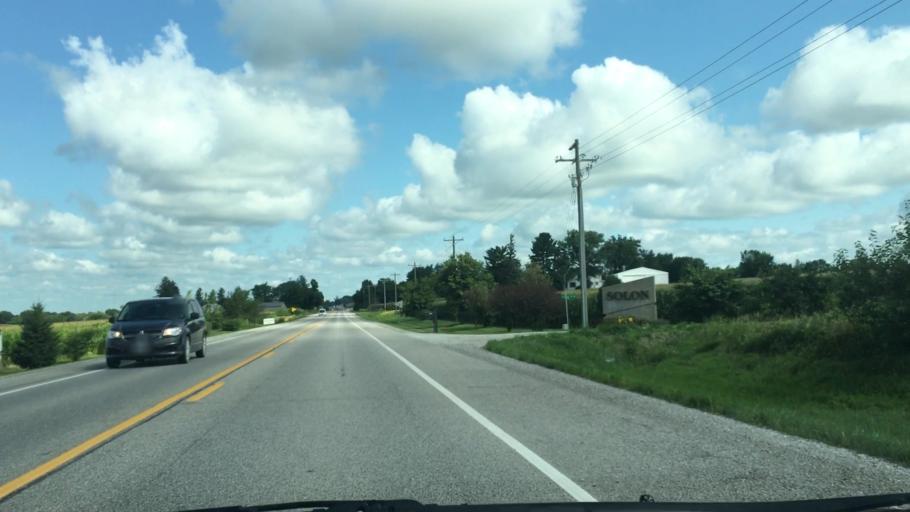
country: US
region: Iowa
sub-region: Johnson County
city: Solon
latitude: 41.7872
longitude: -91.4870
